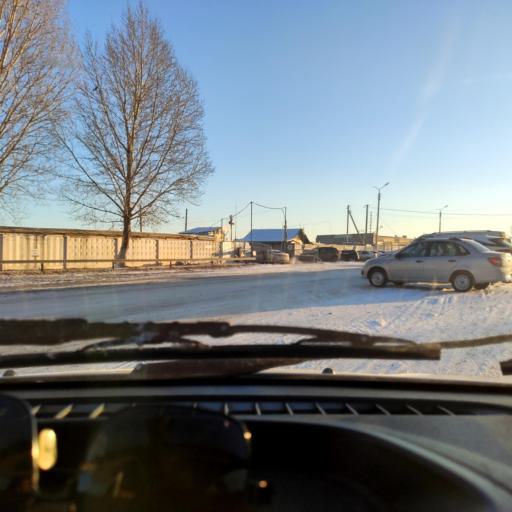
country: RU
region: Samara
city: Tol'yatti
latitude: 53.5692
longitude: 49.4659
